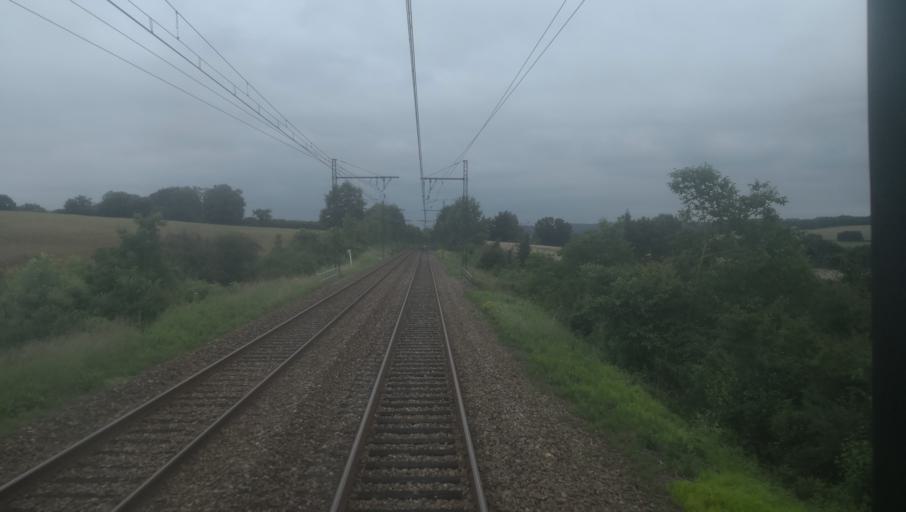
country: FR
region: Centre
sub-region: Departement de l'Indre
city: Le Pechereau
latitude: 46.5353
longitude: 1.5361
